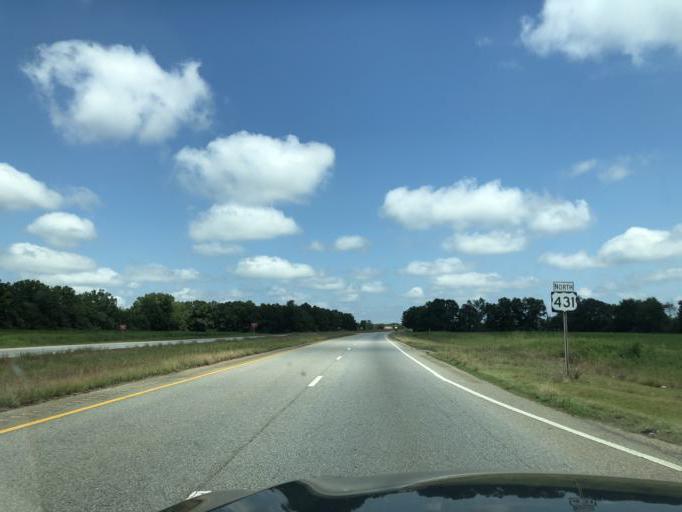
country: US
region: Alabama
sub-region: Henry County
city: Abbeville
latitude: 31.5292
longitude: -85.2911
